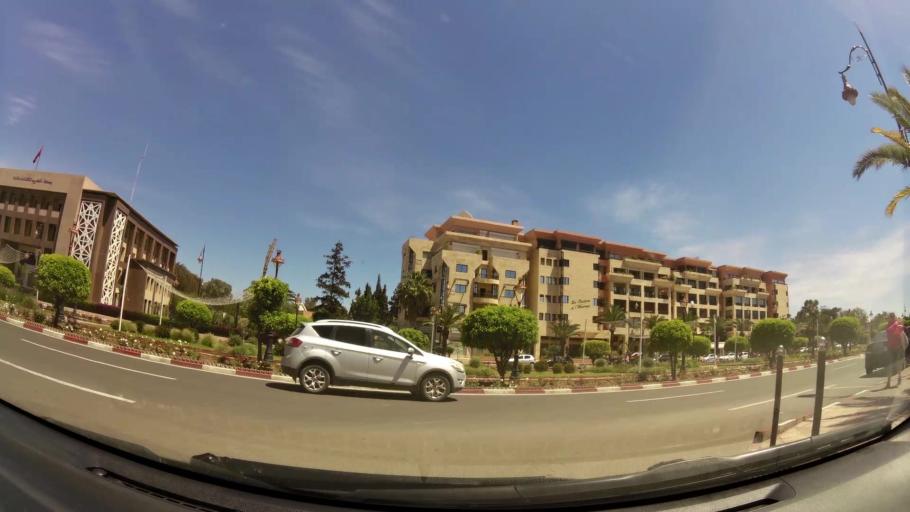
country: MA
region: Marrakech-Tensift-Al Haouz
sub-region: Marrakech
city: Marrakesh
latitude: 31.6212
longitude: -8.0106
